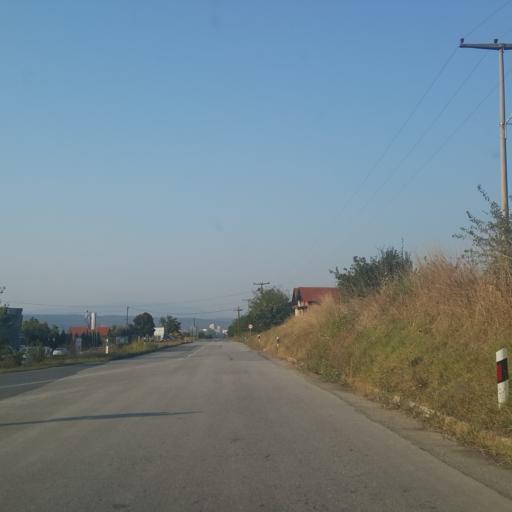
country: RS
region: Central Serbia
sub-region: Zajecarski Okrug
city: Zajecar
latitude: 43.9229
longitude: 22.2943
